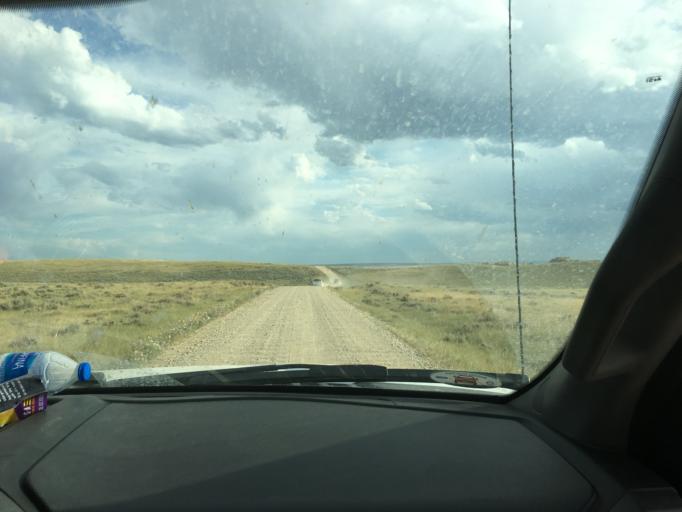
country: US
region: Wyoming
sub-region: Campbell County
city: Wright
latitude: 43.4959
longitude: -105.8595
